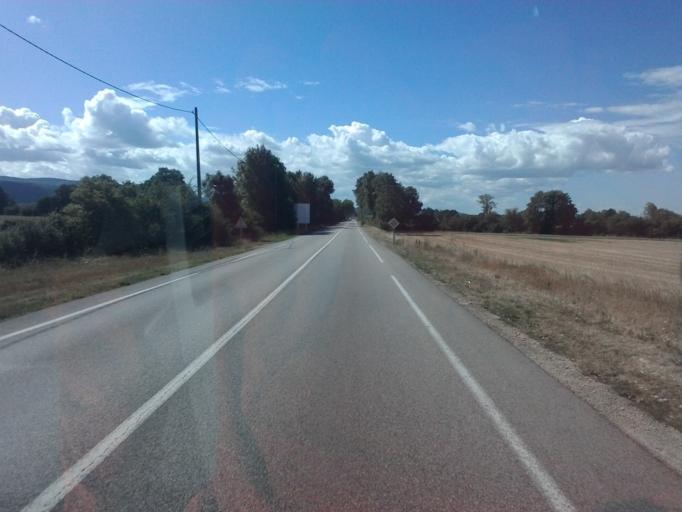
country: FR
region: Rhone-Alpes
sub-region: Departement de l'Ain
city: Ambronay
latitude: 46.0091
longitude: 5.3409
